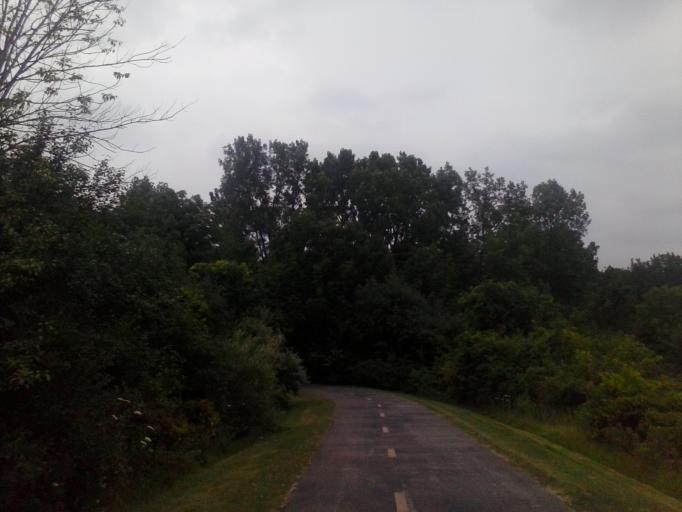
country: US
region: Illinois
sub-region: DuPage County
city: Woodridge
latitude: 41.7566
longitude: -88.0558
